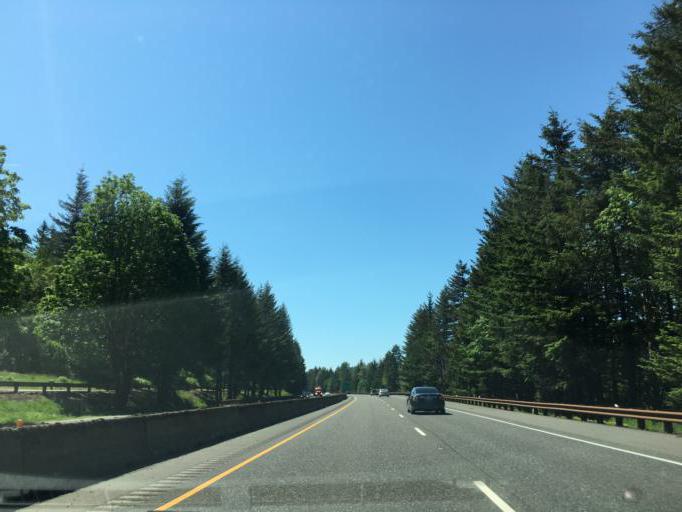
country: US
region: Oregon
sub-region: Hood River County
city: Cascade Locks
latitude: 45.6113
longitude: -122.0224
